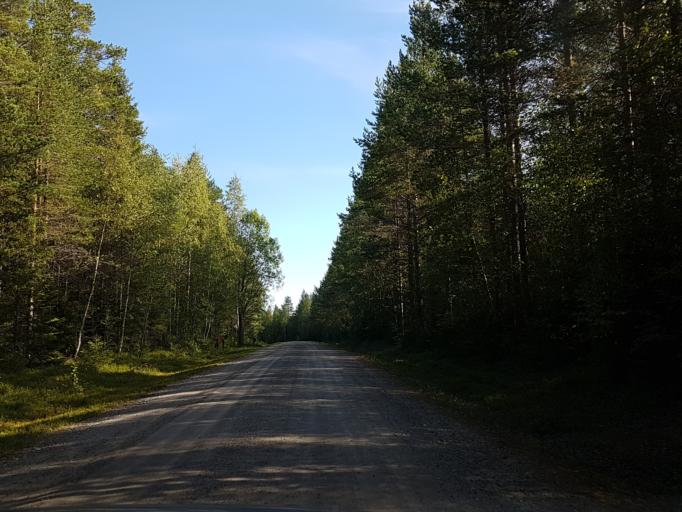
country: SE
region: Vaesterbotten
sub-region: Robertsfors Kommun
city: Robertsfors
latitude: 64.0518
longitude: 20.8714
